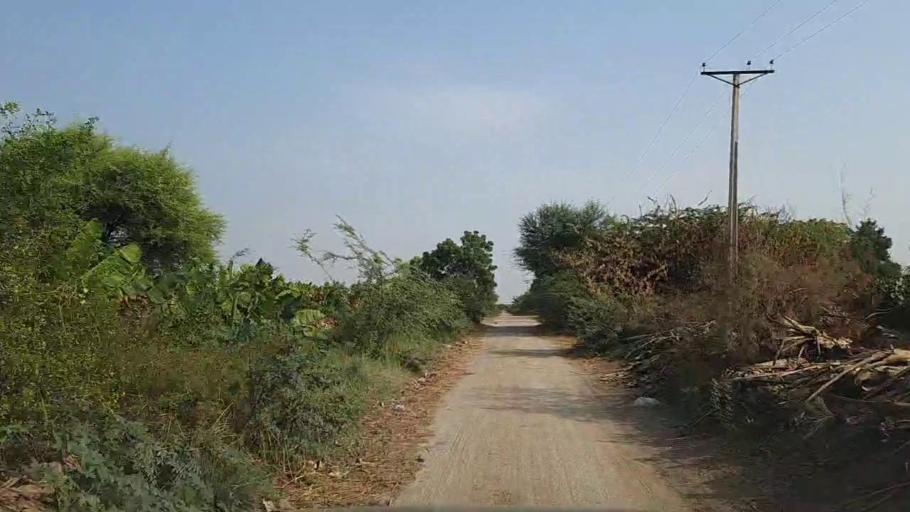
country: PK
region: Sindh
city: Thatta
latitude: 24.6453
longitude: 67.9382
